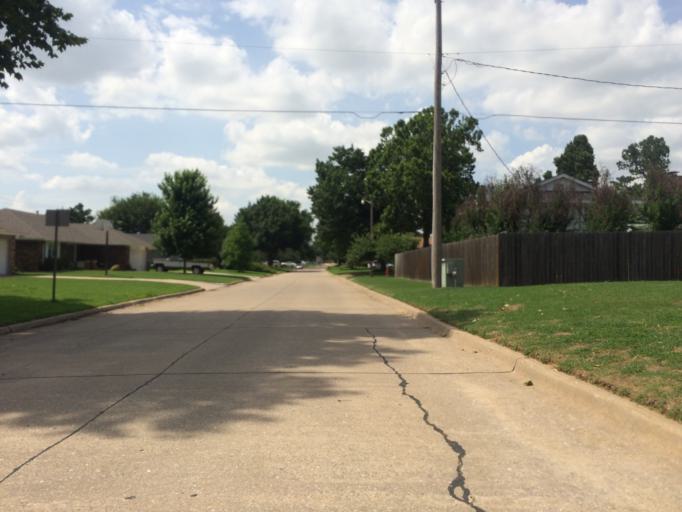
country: US
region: Oklahoma
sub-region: Cleveland County
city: Norman
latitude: 35.2118
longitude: -97.4824
